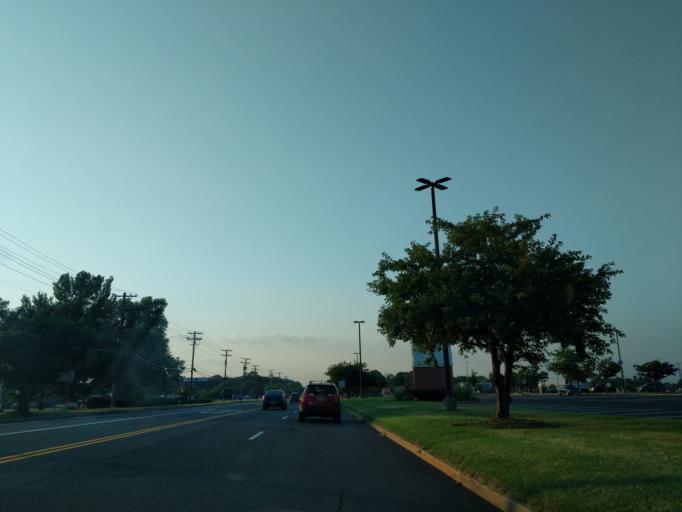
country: US
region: New Jersey
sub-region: Camden County
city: Glendora
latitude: 39.8302
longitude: -75.1006
